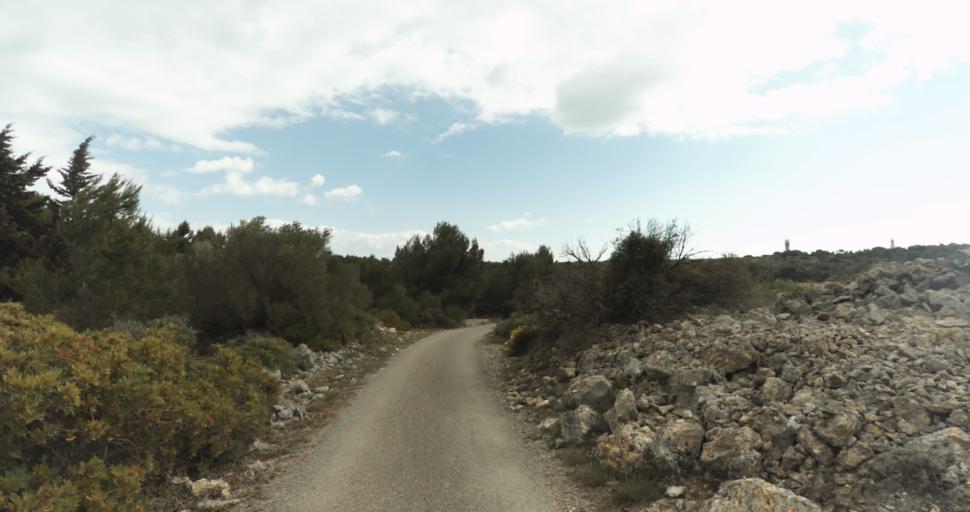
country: FR
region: Languedoc-Roussillon
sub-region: Departement de l'Aude
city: Leucate
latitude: 42.9137
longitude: 3.0476
